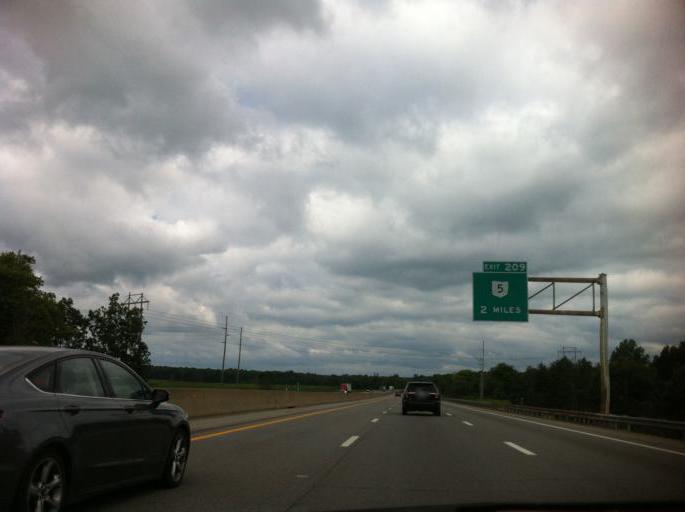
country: US
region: Ohio
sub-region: Trumbull County
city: Newton Falls
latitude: 41.1890
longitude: -80.9367
